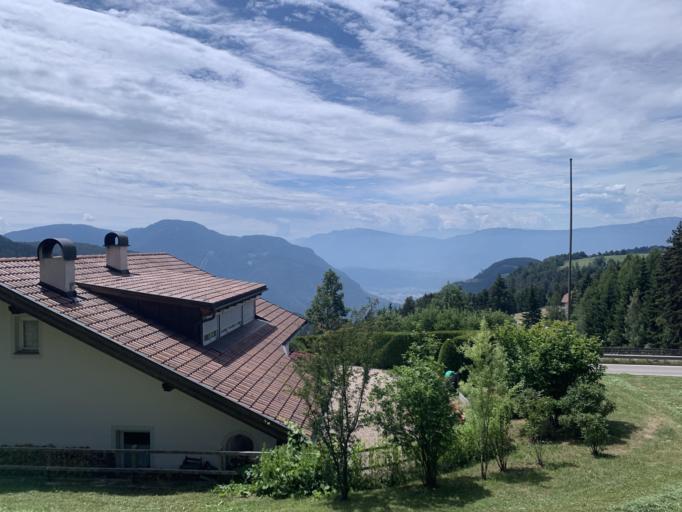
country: IT
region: Trentino-Alto Adige
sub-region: Bolzano
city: Soprabolzano
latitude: 46.5292
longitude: 11.4191
